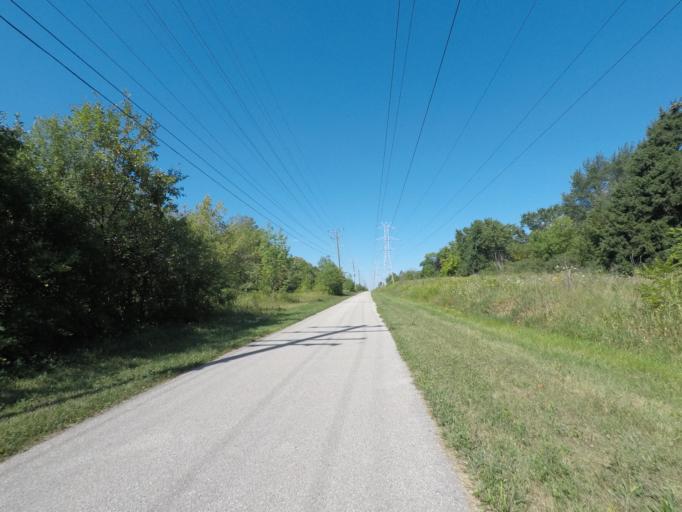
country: US
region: Wisconsin
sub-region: Waukesha County
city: Elm Grove
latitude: 43.0102
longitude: -88.0807
